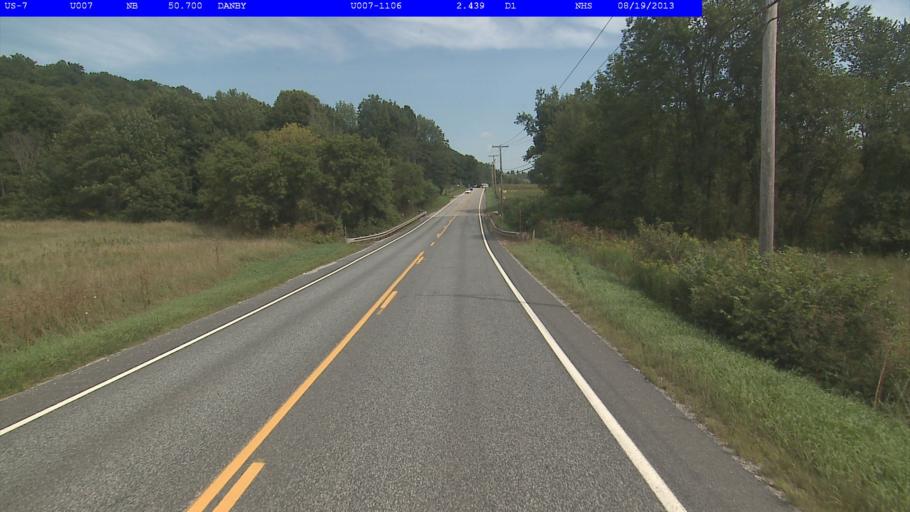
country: US
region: Vermont
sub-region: Rutland County
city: West Rutland
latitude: 43.3970
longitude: -72.9989
